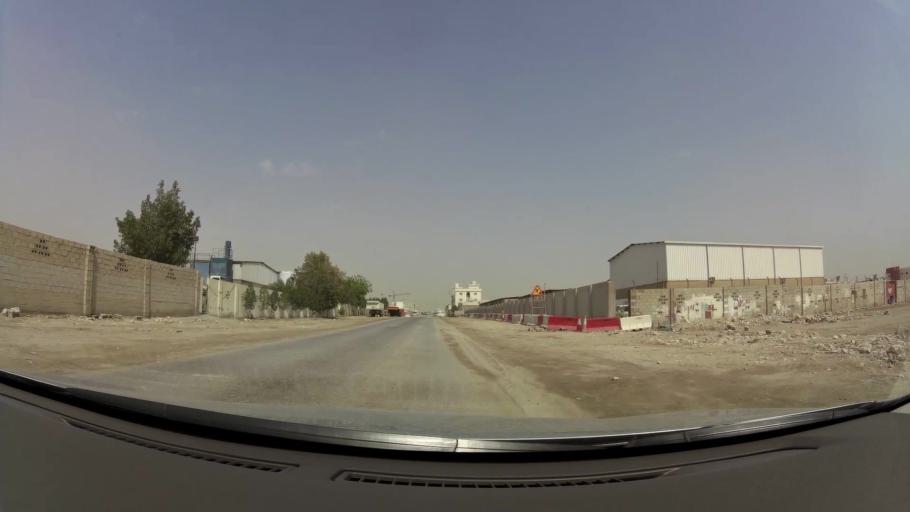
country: QA
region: Al Wakrah
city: Al Wukayr
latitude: 25.1658
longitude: 51.4420
